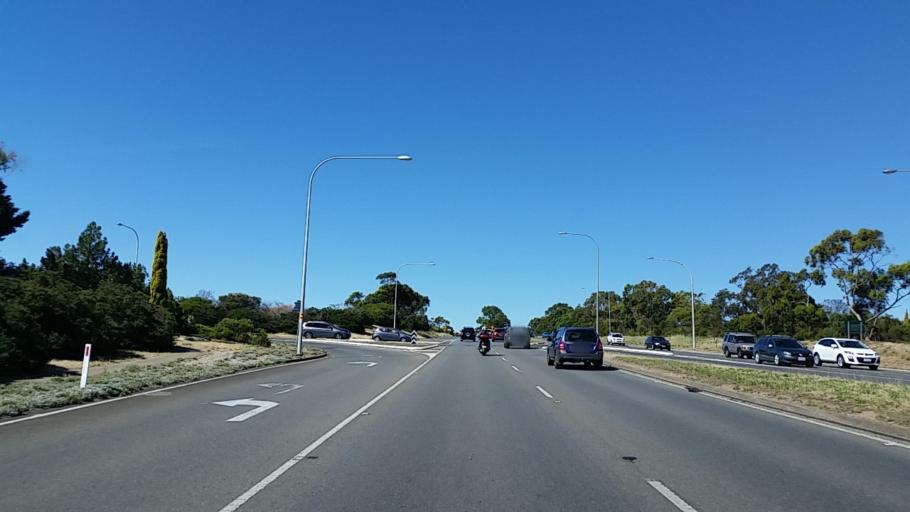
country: AU
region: South Australia
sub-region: Marion
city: Happy Valley
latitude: -35.0703
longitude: 138.5272
